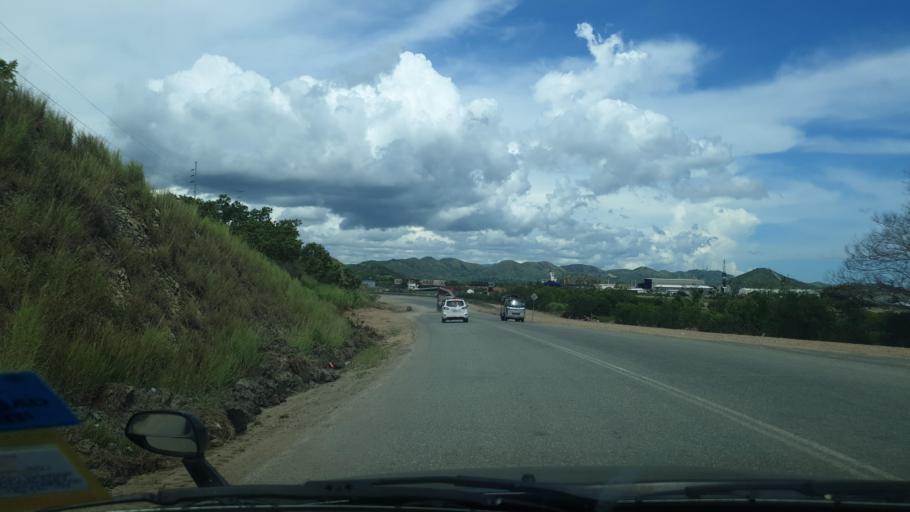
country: PG
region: National Capital
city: Port Moresby
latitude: -9.4199
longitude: 147.0970
